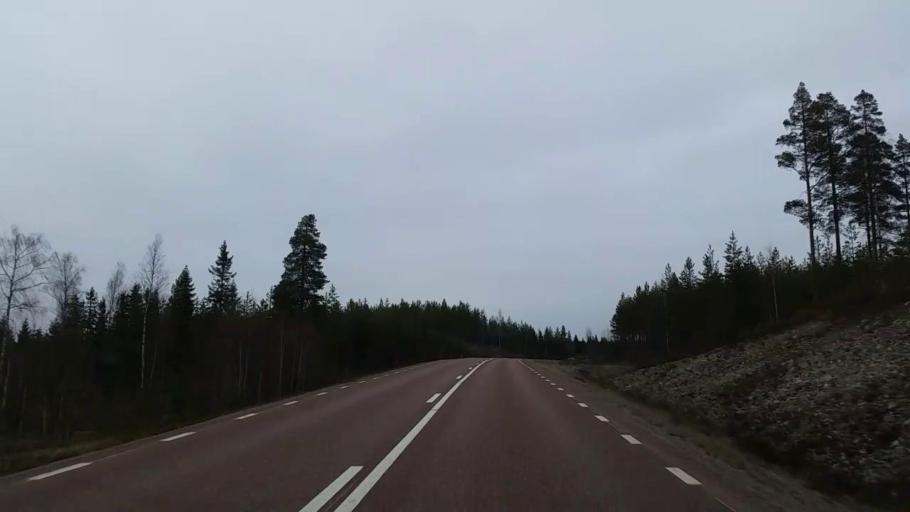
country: SE
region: Gaevleborg
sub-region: Ovanakers Kommun
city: Edsbyn
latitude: 61.2450
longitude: 15.8845
